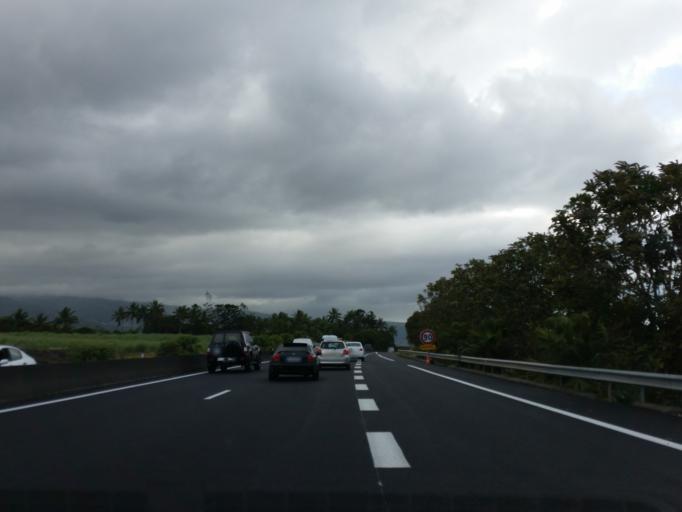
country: RE
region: Reunion
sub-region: Reunion
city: Sainte-Marie
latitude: -20.9030
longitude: 55.5406
